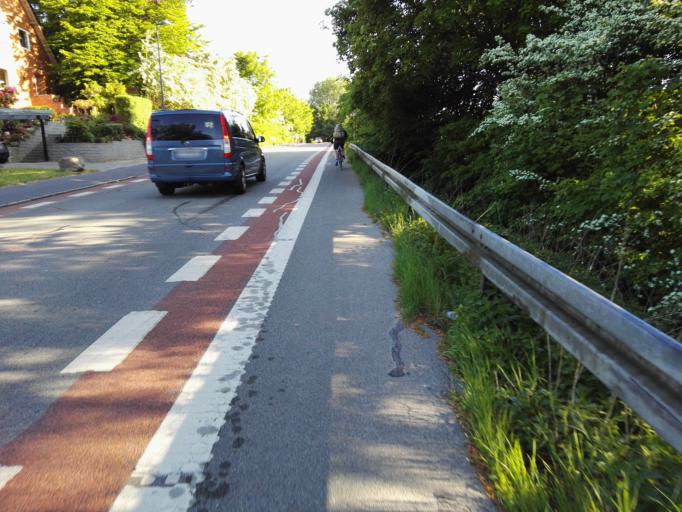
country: DK
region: Capital Region
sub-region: Ballerup Kommune
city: Ballerup
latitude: 55.7426
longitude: 12.3534
